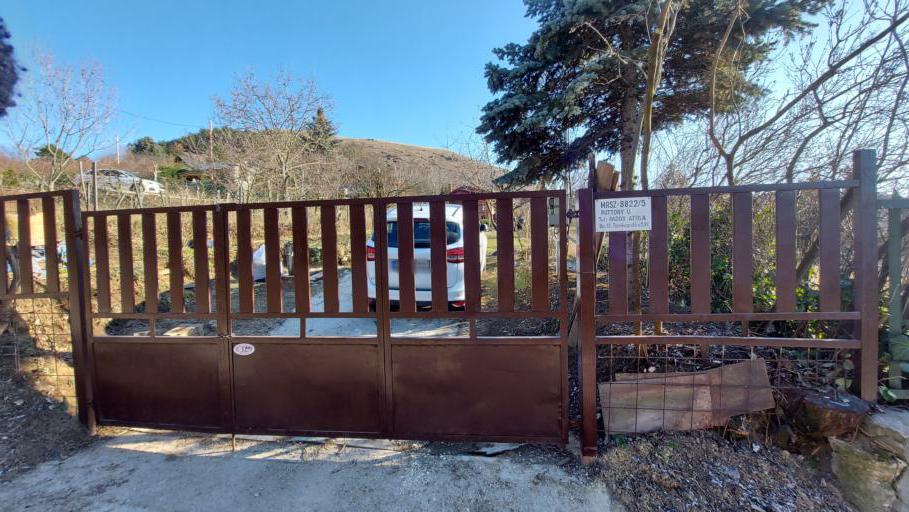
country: HU
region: Pest
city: Budaors
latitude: 47.4694
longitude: 18.9425
